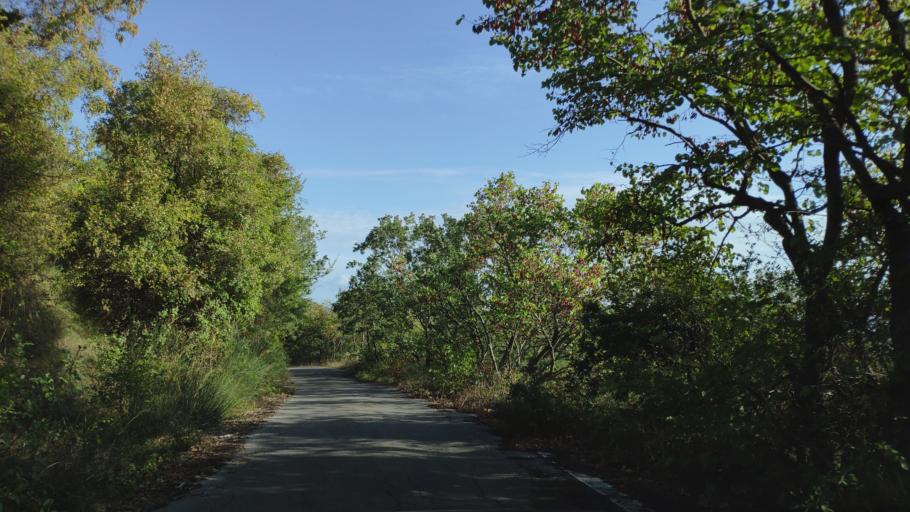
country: GR
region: Peloponnese
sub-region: Nomos Arkadias
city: Dimitsana
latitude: 37.5520
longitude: 22.0405
